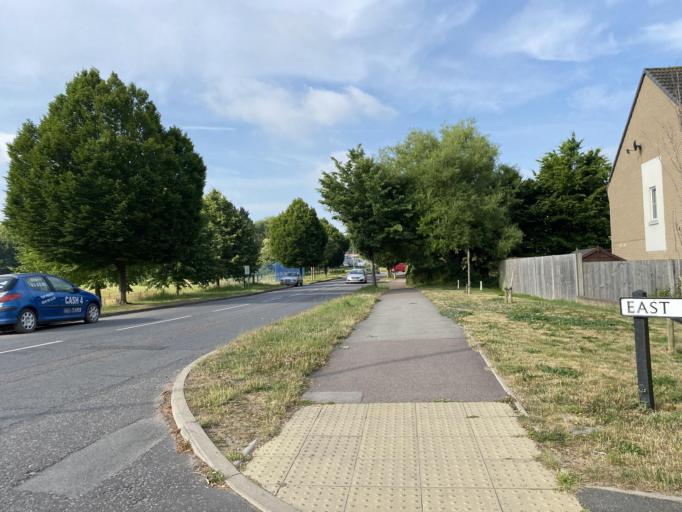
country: GB
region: England
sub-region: Suffolk
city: Haverhill
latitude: 52.0758
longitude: 0.4540
